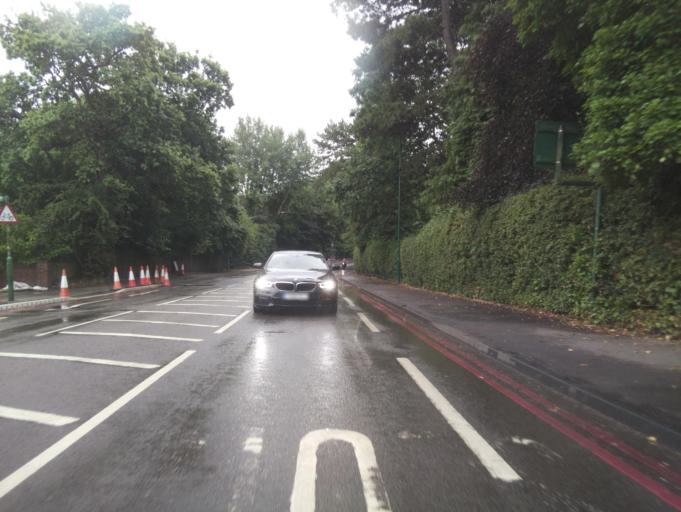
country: GB
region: England
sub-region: Solihull
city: Solihull
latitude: 52.4116
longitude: -1.7925
